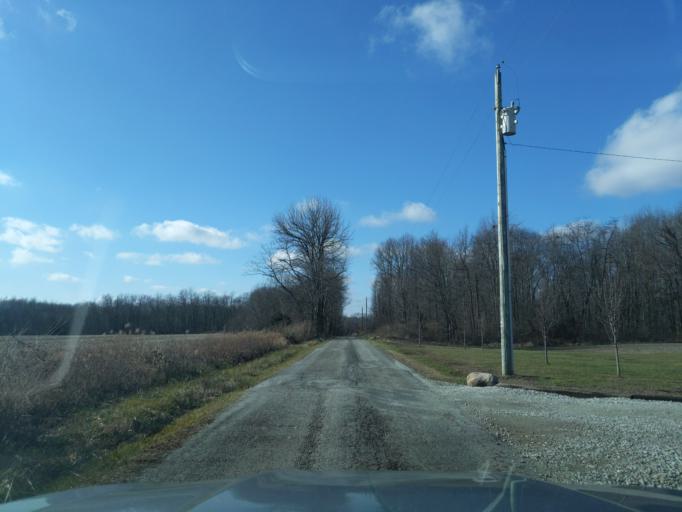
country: US
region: Indiana
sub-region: Decatur County
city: Greensburg
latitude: 39.2410
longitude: -85.4535
